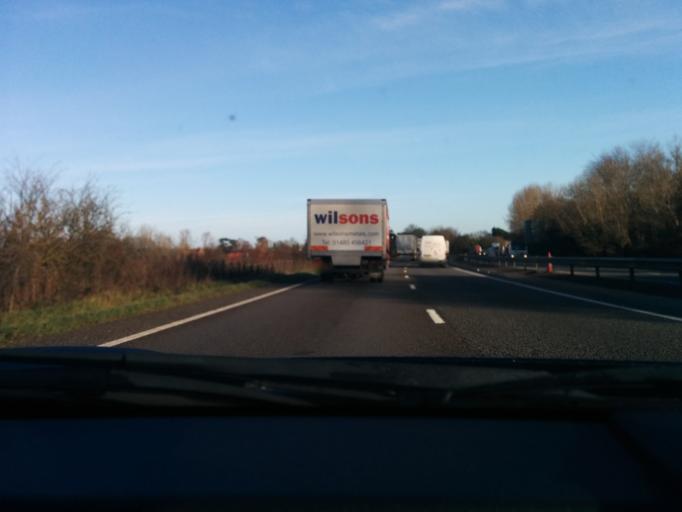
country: GB
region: England
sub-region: Oxfordshire
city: Abingdon
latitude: 51.6755
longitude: -1.3062
